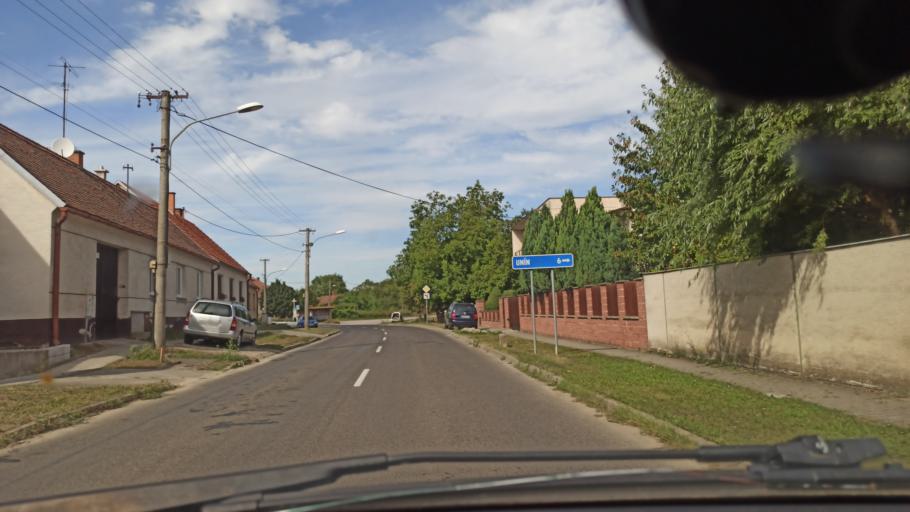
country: SK
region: Trnavsky
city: Gbely
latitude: 48.6843
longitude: 17.2015
